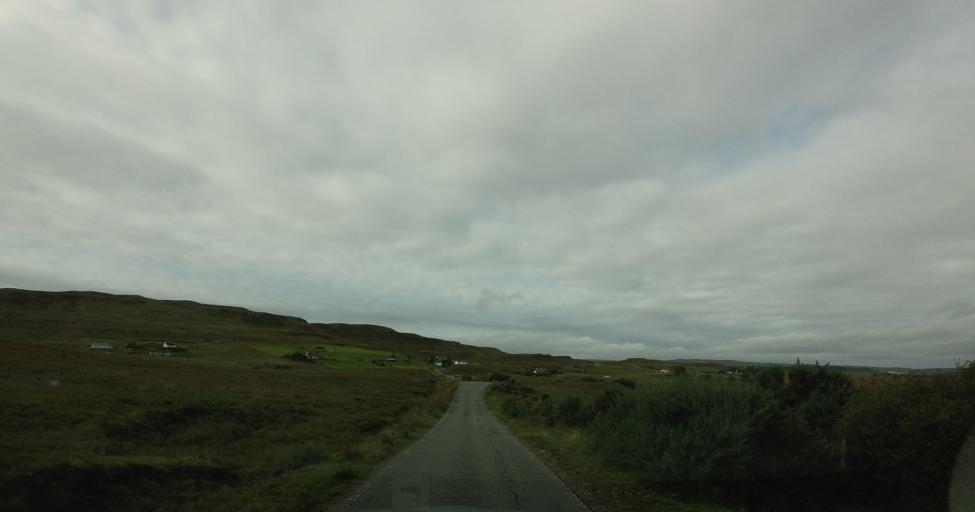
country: GB
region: Scotland
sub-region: Highland
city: Portree
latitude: 57.4212
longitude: -6.2531
